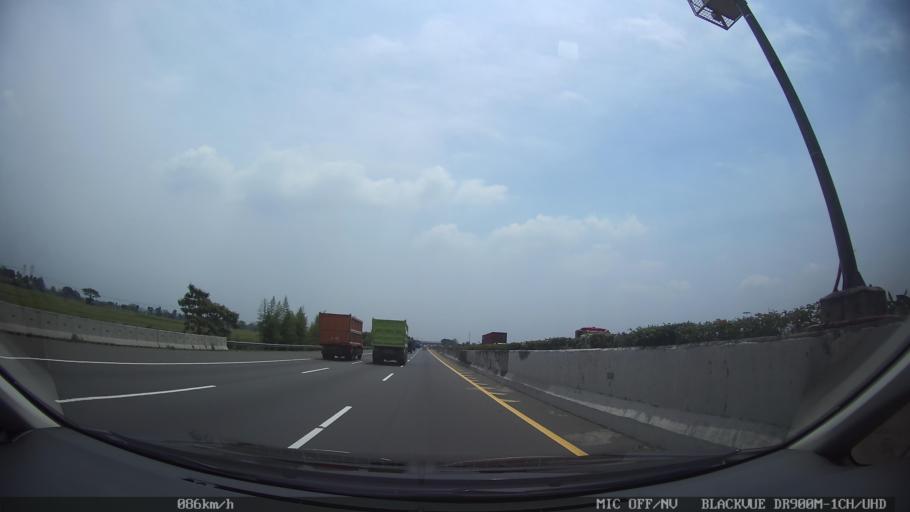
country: ID
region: West Java
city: Kresek
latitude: -6.1771
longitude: 106.3737
